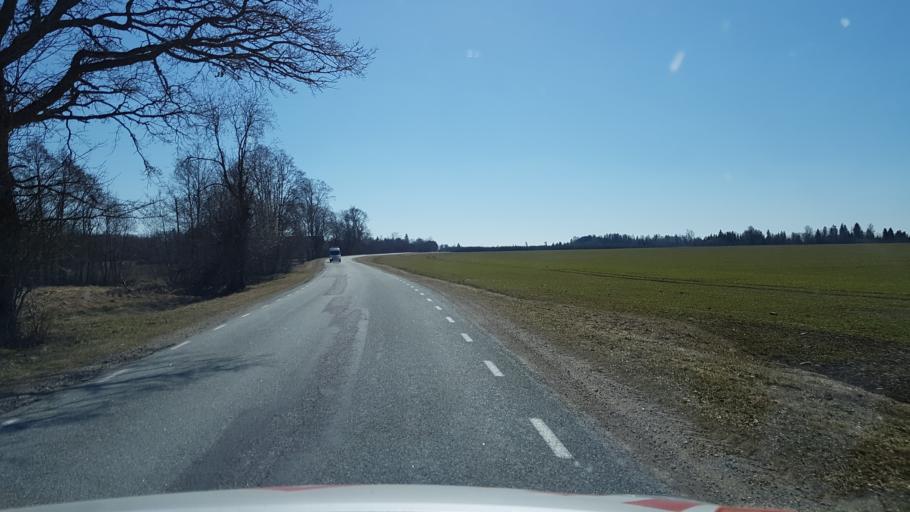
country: EE
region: Laeaene-Virumaa
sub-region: Rakke vald
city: Rakke
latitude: 59.0331
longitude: 26.3482
